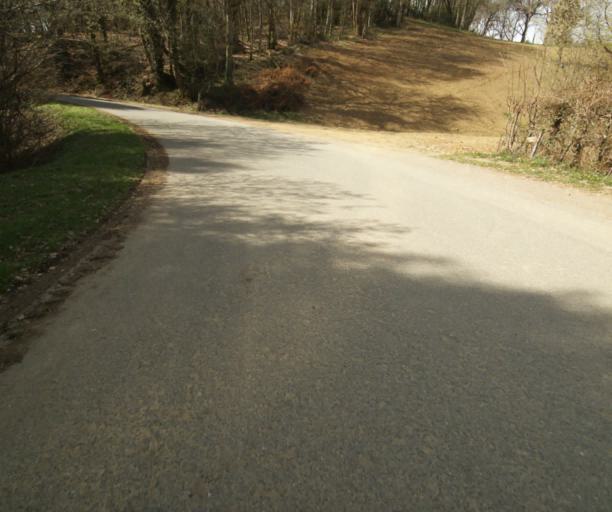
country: FR
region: Limousin
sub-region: Departement de la Correze
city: Naves
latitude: 45.3625
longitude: 1.7983
